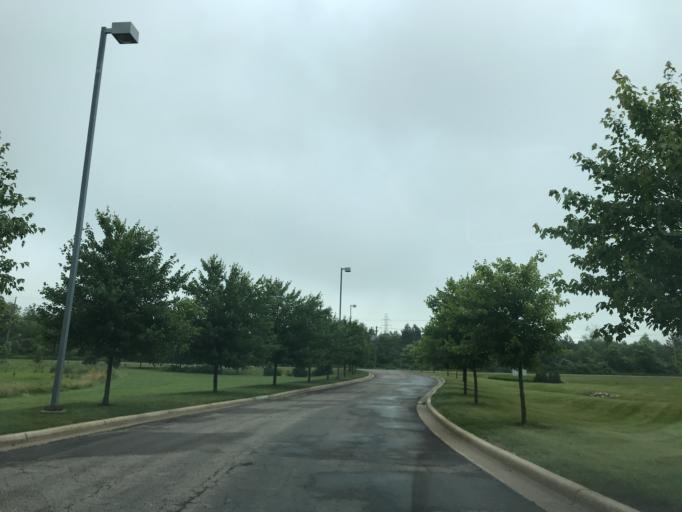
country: US
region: Michigan
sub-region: Washtenaw County
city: Ypsilanti
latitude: 42.2736
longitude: -83.6270
